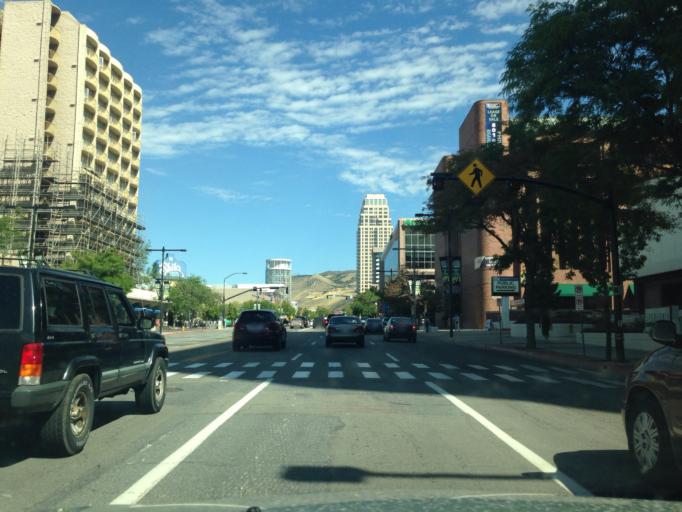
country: US
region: Utah
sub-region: Salt Lake County
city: Salt Lake City
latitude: 40.7638
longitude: -111.8939
